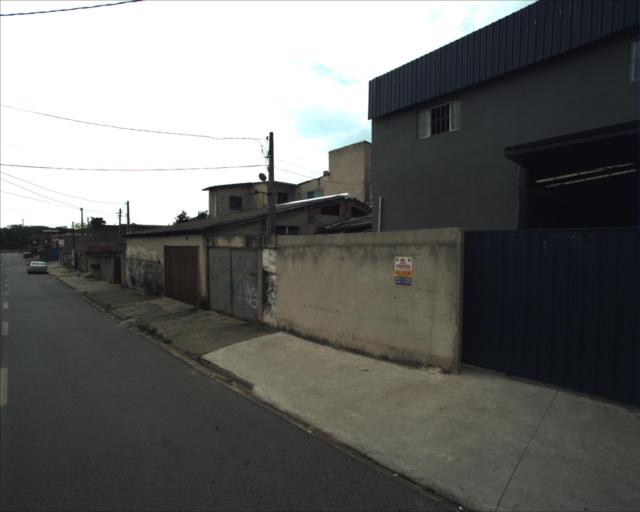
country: BR
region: Sao Paulo
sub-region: Sorocaba
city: Sorocaba
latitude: -23.4621
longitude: -47.4417
